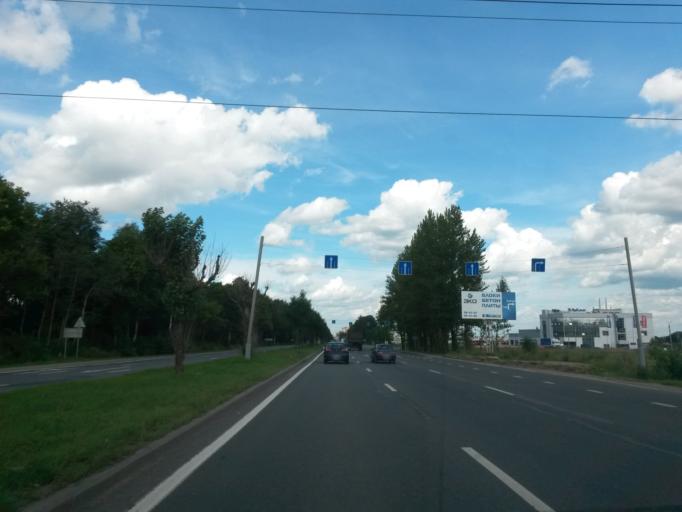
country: RU
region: Jaroslavl
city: Krasnyye Tkachi
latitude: 57.5562
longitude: 39.8174
